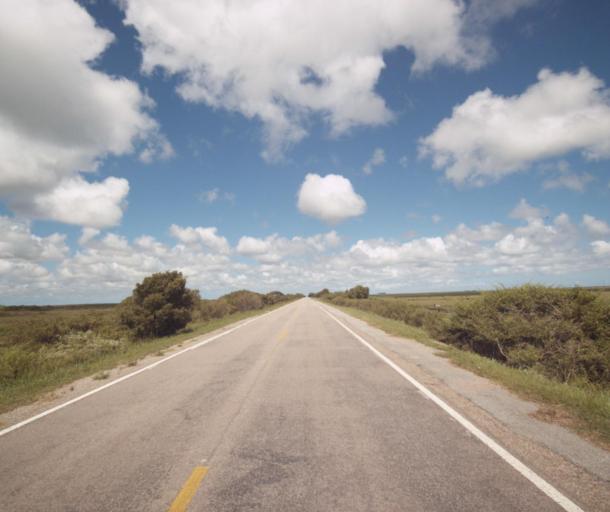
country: BR
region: Rio Grande do Sul
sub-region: Arroio Grande
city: Arroio Grande
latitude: -32.5442
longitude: -52.5420
